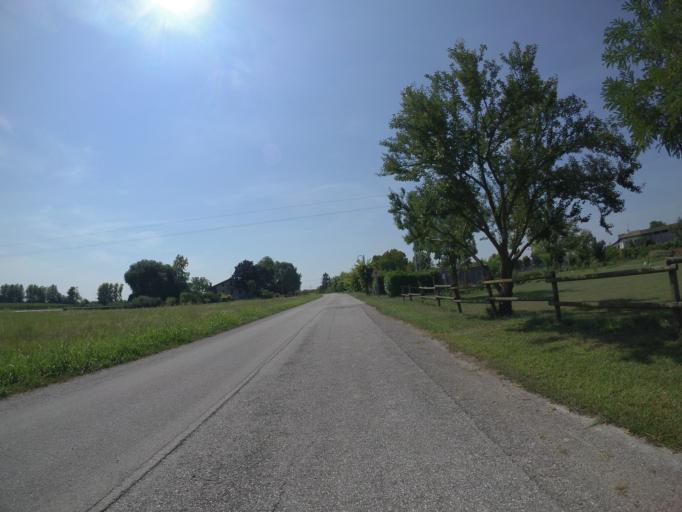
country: IT
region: Friuli Venezia Giulia
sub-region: Provincia di Udine
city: Varmo
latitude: 45.9189
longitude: 12.9936
